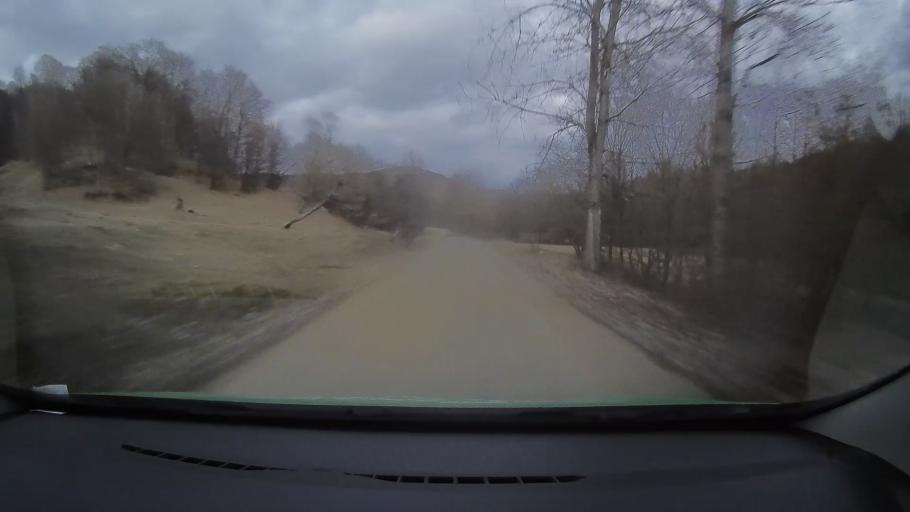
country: RO
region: Prahova
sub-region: Comuna Adunati
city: Adunati
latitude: 45.1215
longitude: 25.6001
